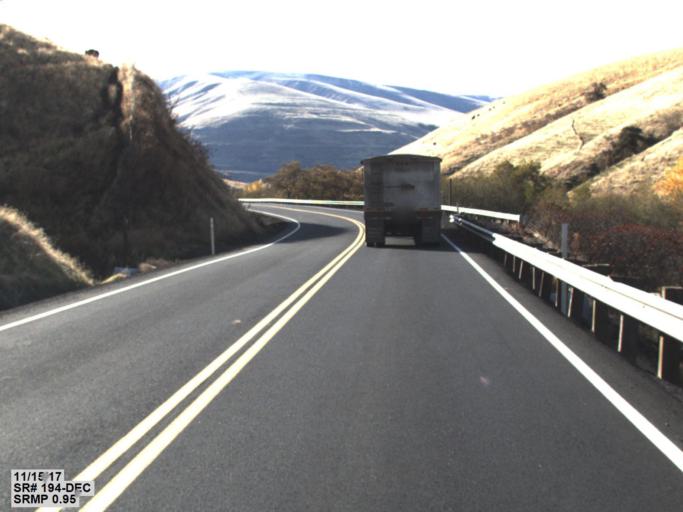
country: US
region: Washington
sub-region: Whitman County
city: Colfax
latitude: 46.7158
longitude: -117.4659
